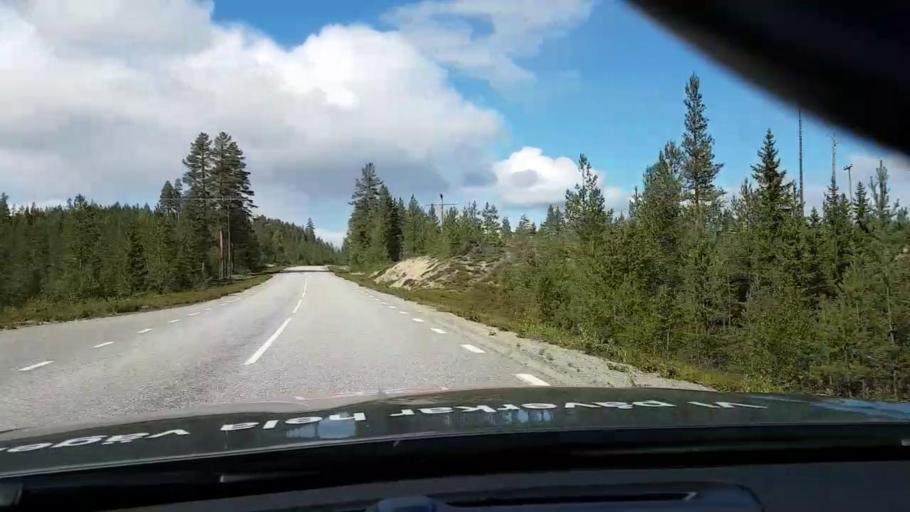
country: SE
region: Vaesternorrland
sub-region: OErnskoeldsviks Kommun
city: Bredbyn
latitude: 63.6687
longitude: 17.8282
